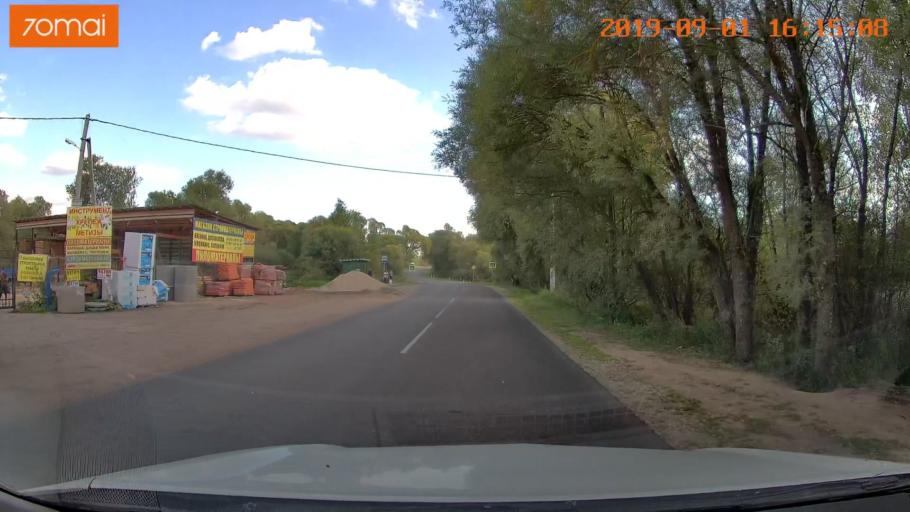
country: RU
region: Kaluga
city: Maloyaroslavets
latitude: 54.9249
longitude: 36.4749
